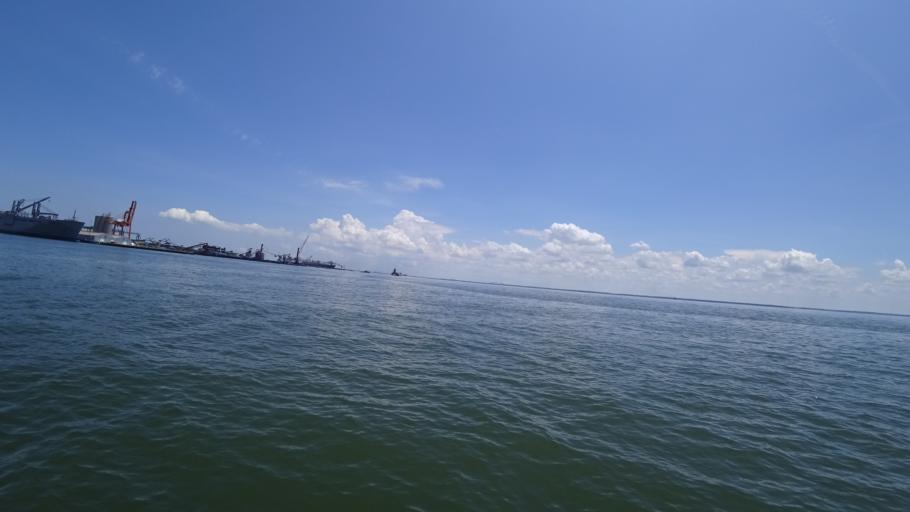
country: US
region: Virginia
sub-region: City of Newport News
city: Newport News
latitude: 36.9694
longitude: -76.4394
